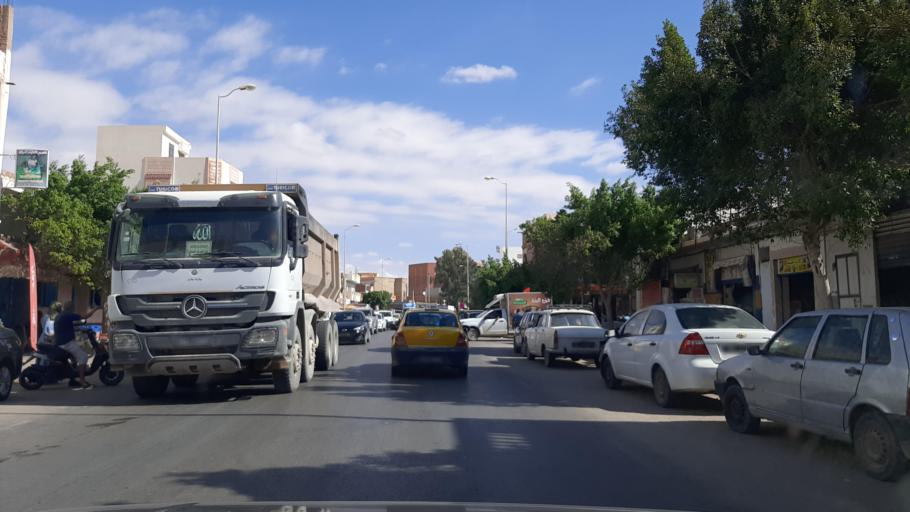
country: TN
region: Tataouine
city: Tataouine
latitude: 32.9288
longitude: 10.4462
